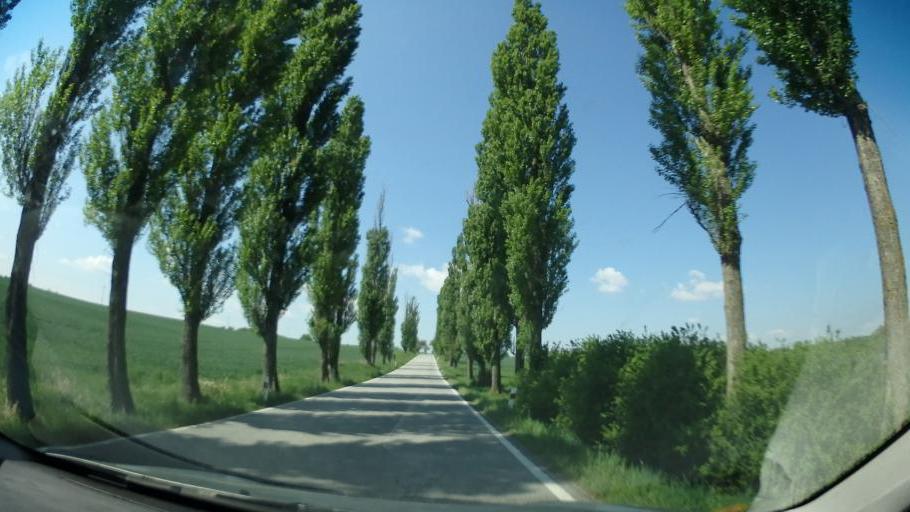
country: CZ
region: Vysocina
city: Namest' nad Oslavou
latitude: 49.2083
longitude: 16.1164
